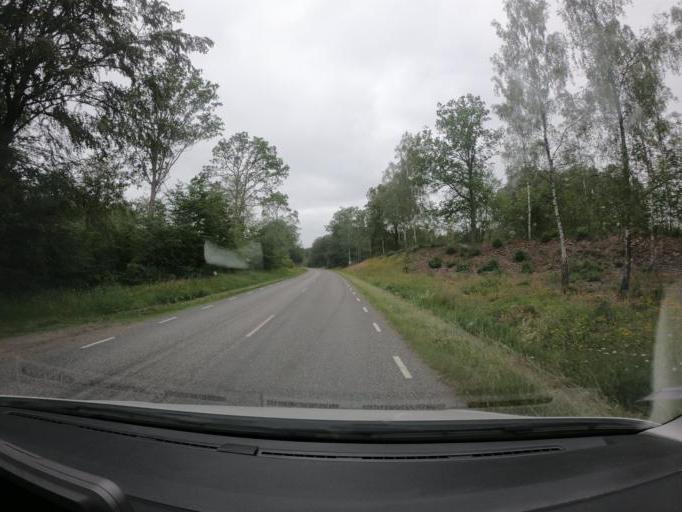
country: SE
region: Skane
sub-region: Perstorps Kommun
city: Perstorp
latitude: 56.1166
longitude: 13.4131
